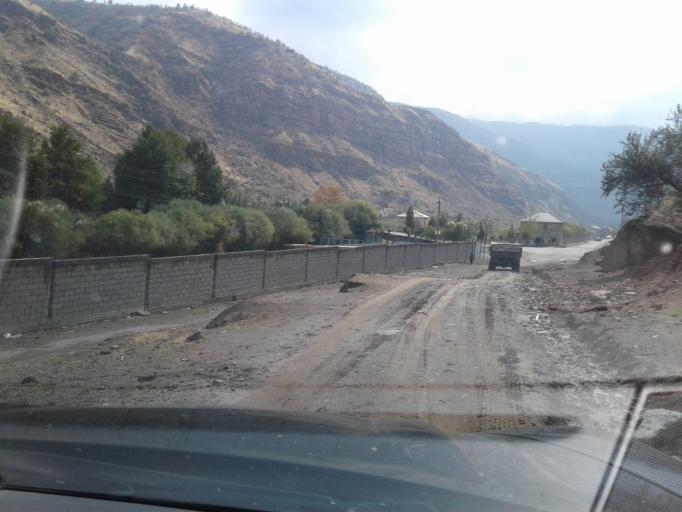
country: TJ
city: Shahrinav
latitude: 38.6953
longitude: 68.3692
